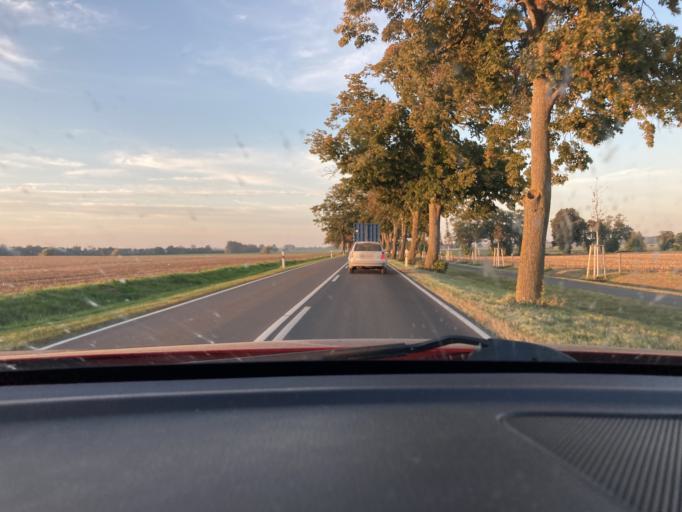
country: DE
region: Mecklenburg-Vorpommern
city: Anklam
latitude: 53.7888
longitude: 13.6630
